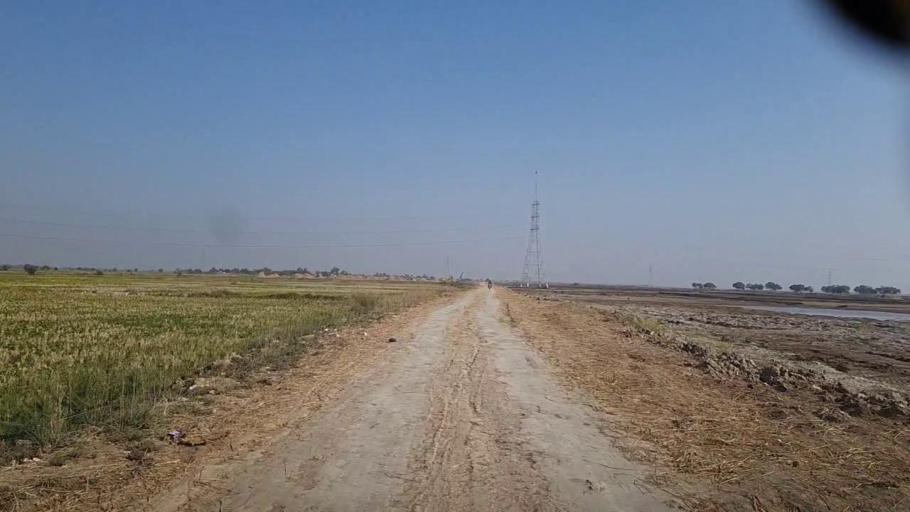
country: PK
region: Sindh
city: Jacobabad
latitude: 28.3076
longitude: 68.5930
